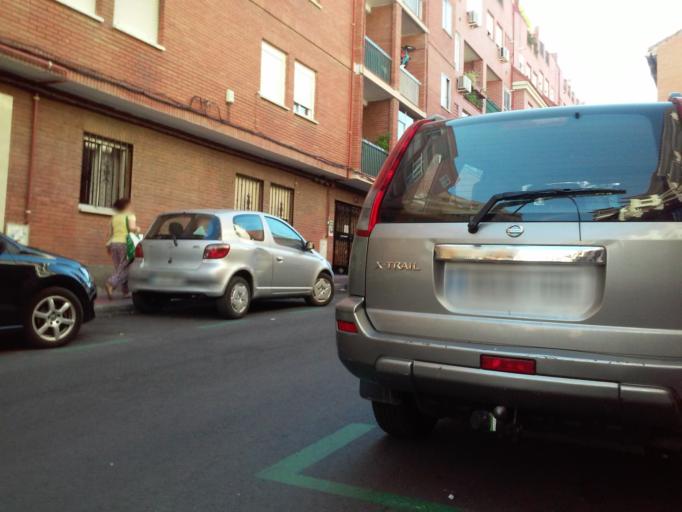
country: ES
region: Madrid
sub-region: Provincia de Madrid
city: Valdemoro
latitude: 40.1919
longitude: -3.6800
